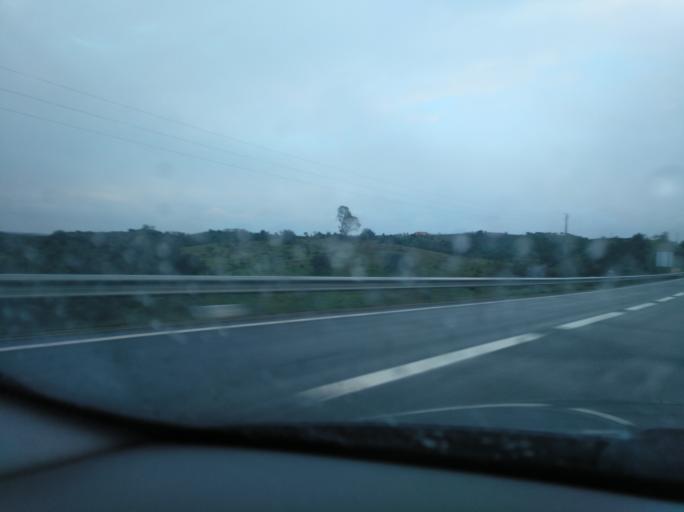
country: PT
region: Faro
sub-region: Castro Marim
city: Castro Marim
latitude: 37.3000
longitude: -7.4887
